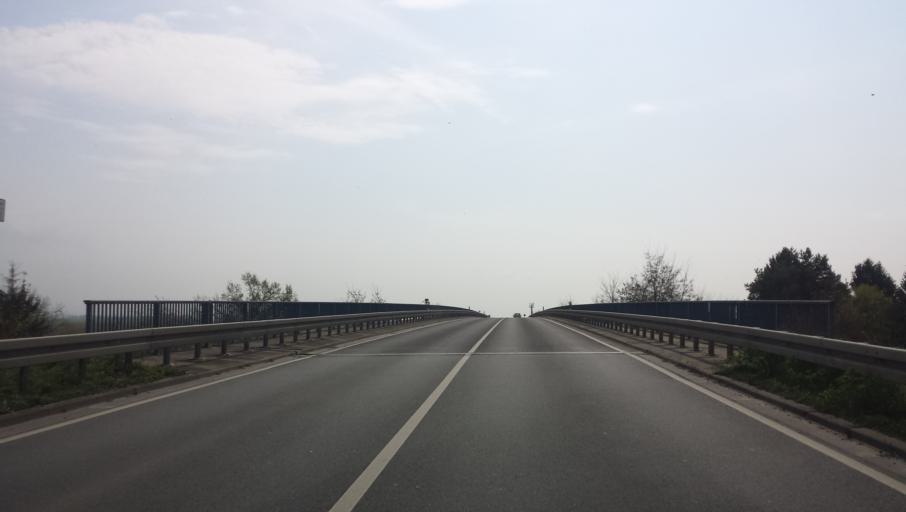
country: DE
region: Hesse
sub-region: Regierungsbezirk Darmstadt
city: Stockstadt am Rhein
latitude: 49.8217
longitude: 8.4797
